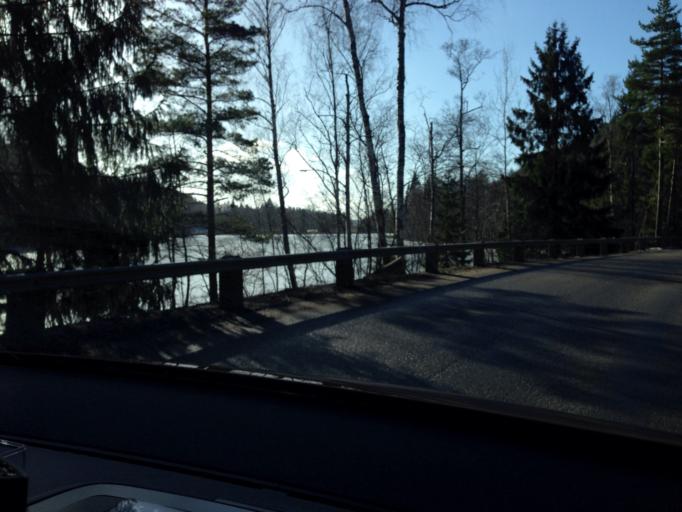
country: SE
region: Stockholm
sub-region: Botkyrka Kommun
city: Varsta
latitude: 59.1501
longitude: 17.7963
